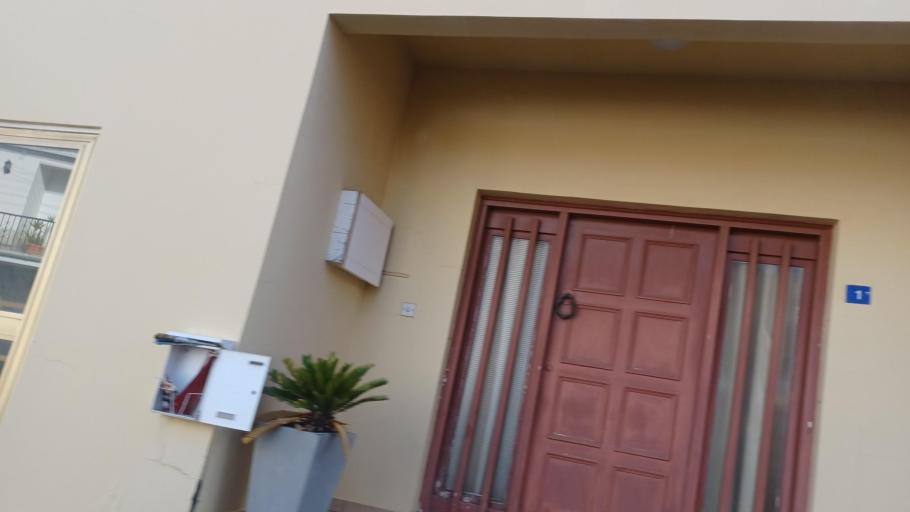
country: CY
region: Lefkosia
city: Lythrodontas
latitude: 34.9498
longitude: 33.2939
